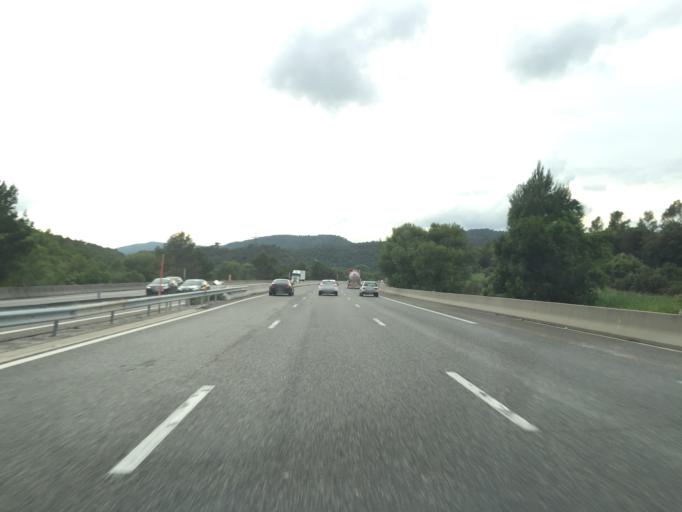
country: FR
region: Provence-Alpes-Cote d'Azur
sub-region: Departement du Var
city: Camps-la-Source
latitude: 43.4164
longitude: 6.1274
